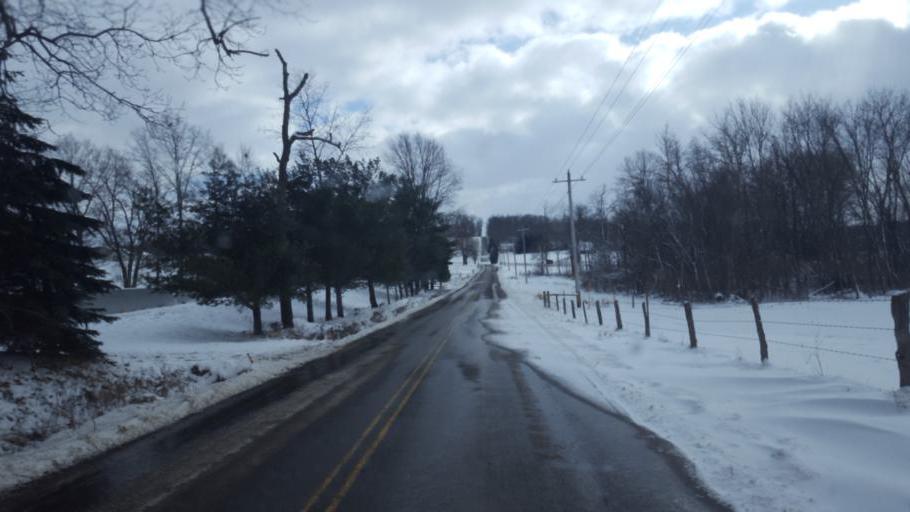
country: US
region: Ohio
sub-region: Knox County
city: Danville
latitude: 40.5289
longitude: -82.3610
